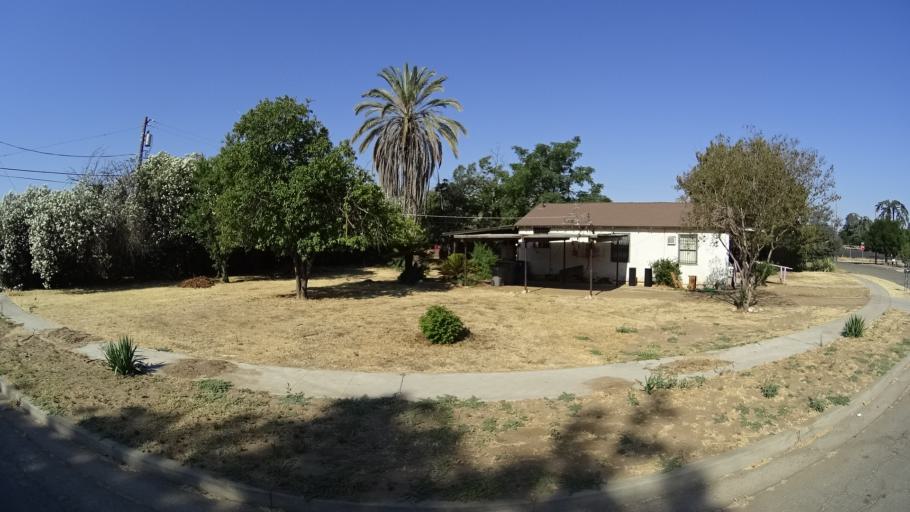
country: US
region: California
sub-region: Fresno County
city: West Park
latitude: 36.7266
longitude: -119.8213
